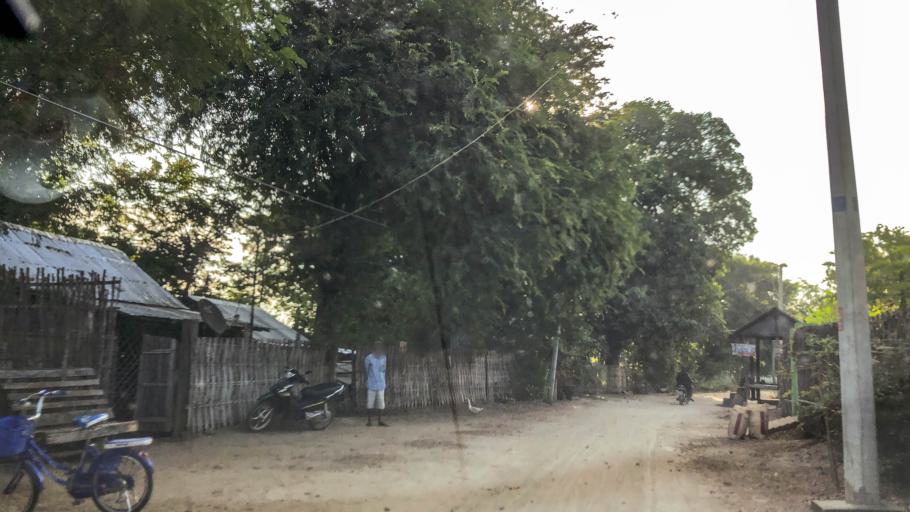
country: MM
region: Magway
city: Magway
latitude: 19.9766
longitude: 95.0342
